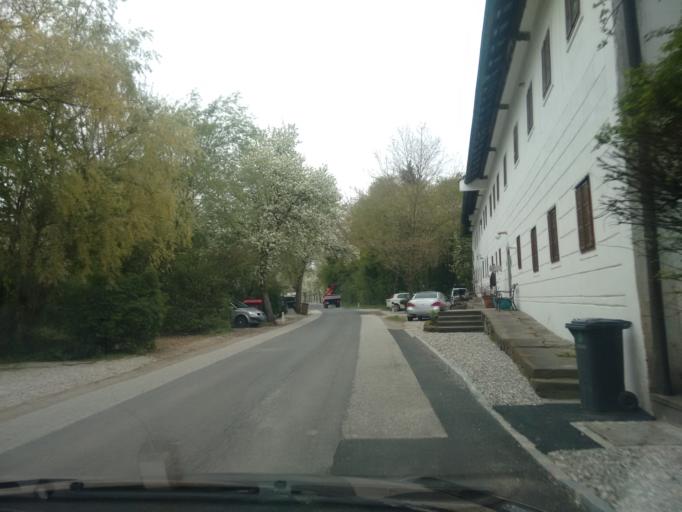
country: AT
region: Upper Austria
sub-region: Wels-Land
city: Buchkirchen
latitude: 48.2102
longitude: 13.9876
